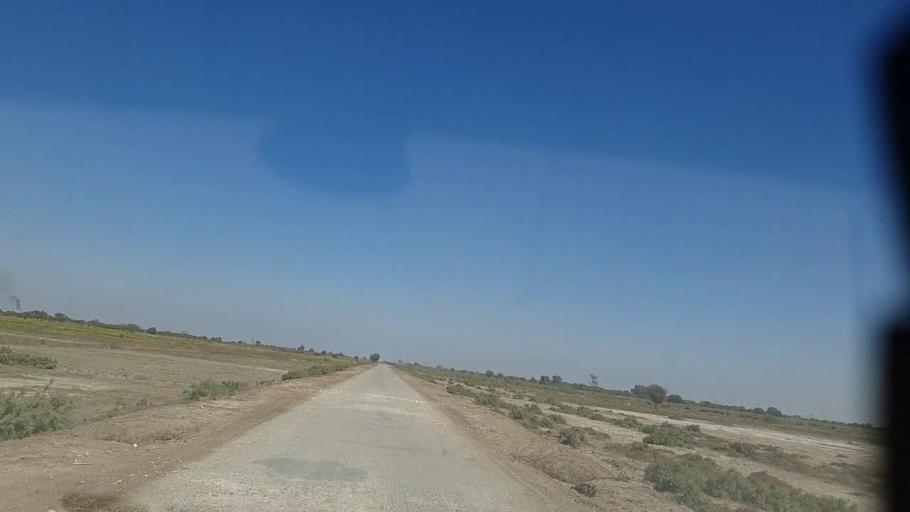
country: PK
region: Sindh
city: Mirwah Gorchani
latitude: 25.2630
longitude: 69.0528
